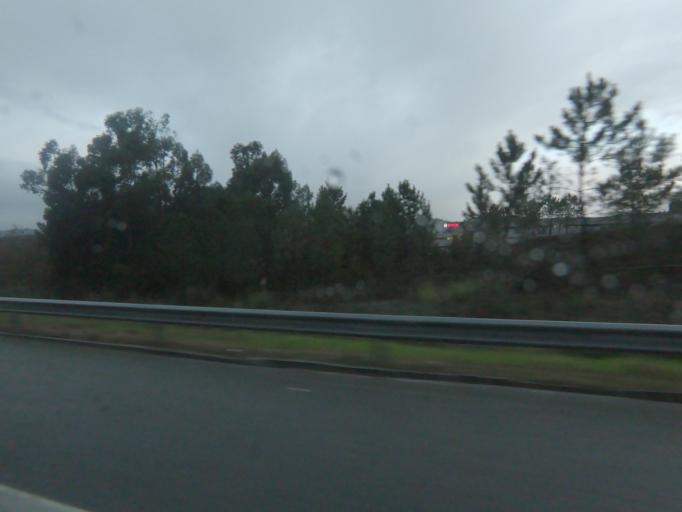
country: PT
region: Braga
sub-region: Braga
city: Oliveira
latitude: 41.5314
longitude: -8.4861
